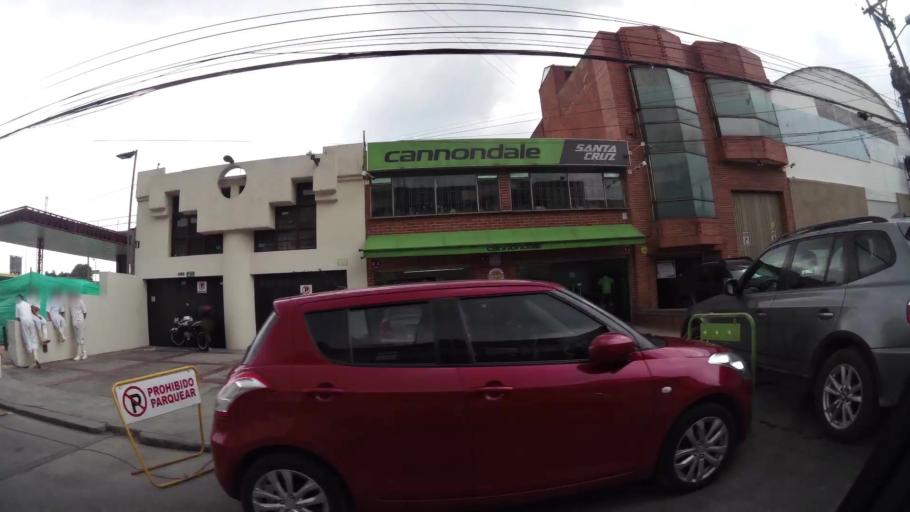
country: CO
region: Cundinamarca
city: Cota
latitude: 4.7475
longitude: -74.0461
